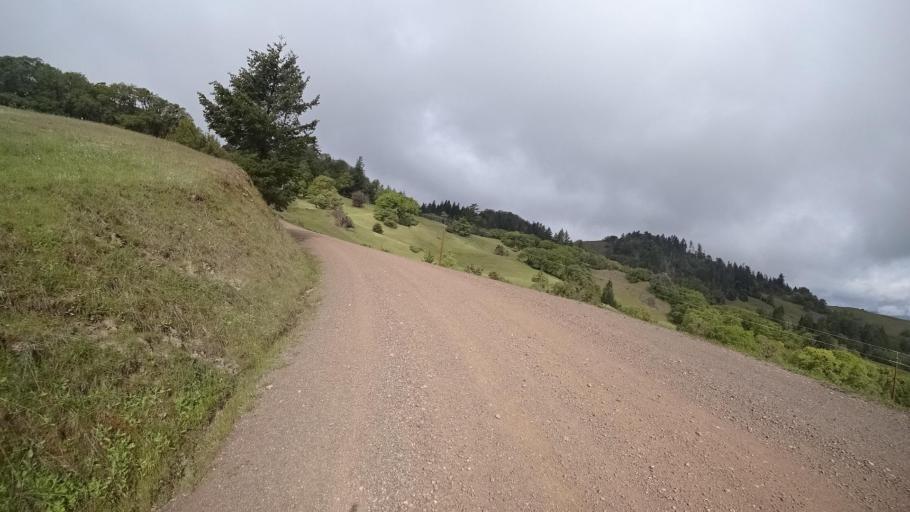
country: US
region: California
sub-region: Humboldt County
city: Redway
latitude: 40.2011
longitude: -123.6965
